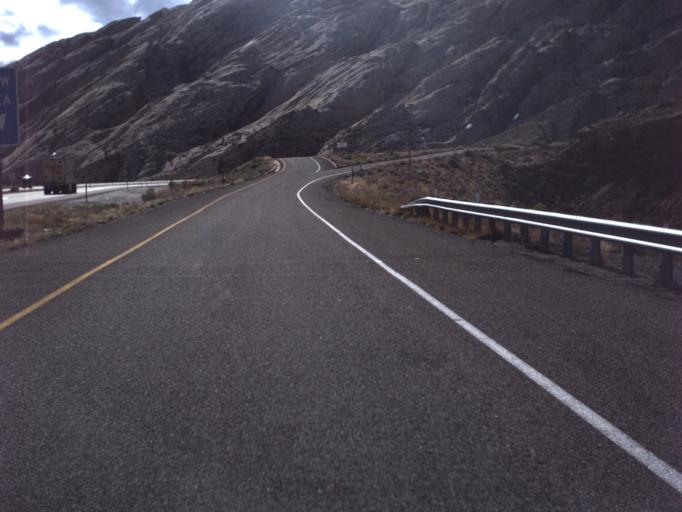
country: US
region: Utah
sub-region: Carbon County
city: East Carbon City
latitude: 38.9217
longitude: -110.4279
